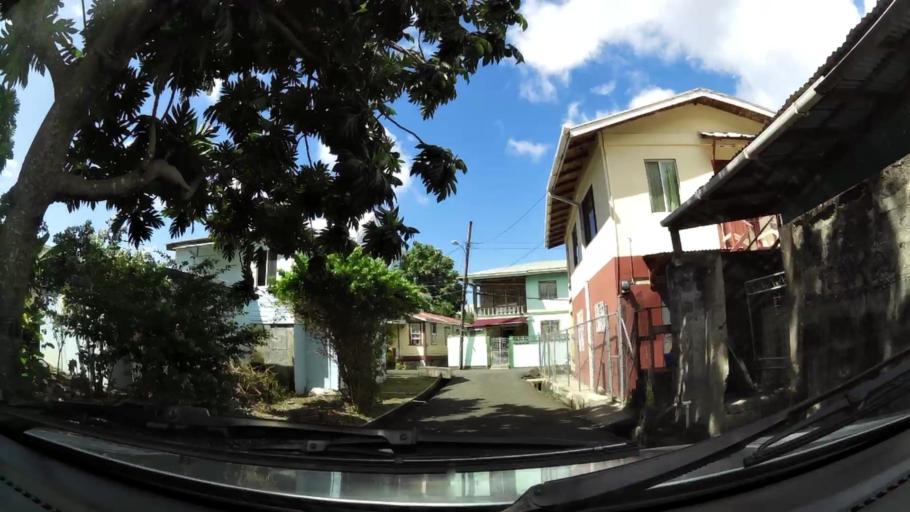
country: GD
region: Saint John
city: Gouyave
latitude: 12.1671
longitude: -61.7287
